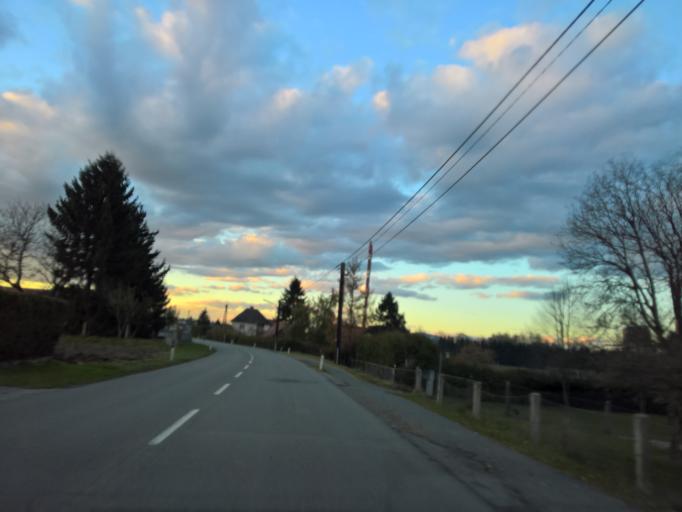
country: AT
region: Styria
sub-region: Politischer Bezirk Leibnitz
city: Weitendorf
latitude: 46.9023
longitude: 15.4850
